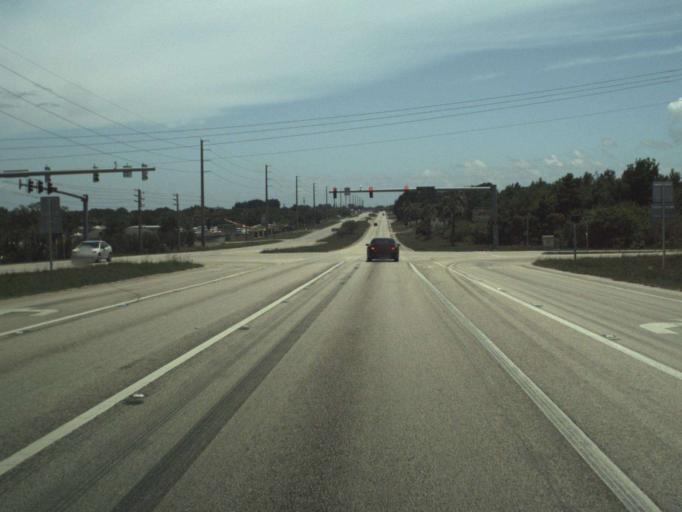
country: US
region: Florida
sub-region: Saint Lucie County
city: Fort Pierce North
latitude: 27.4992
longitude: -80.3458
